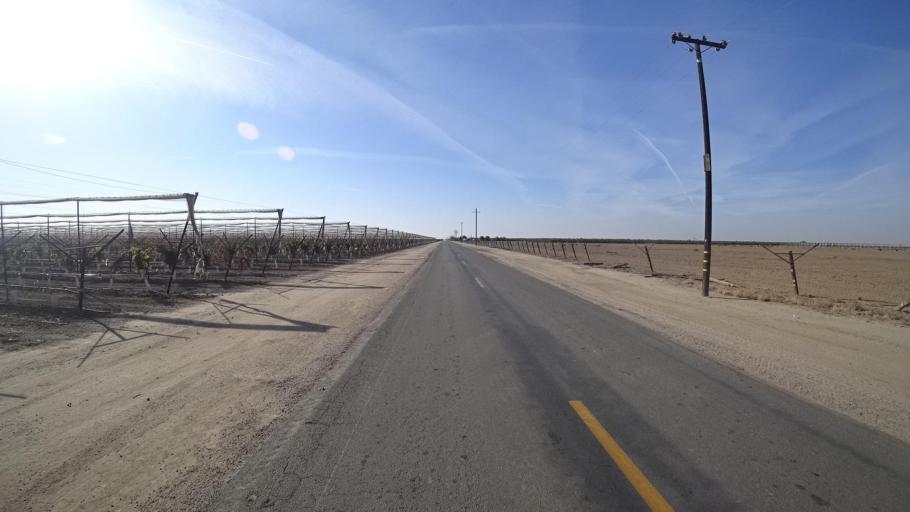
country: US
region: California
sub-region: Kern County
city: McFarland
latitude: 35.7035
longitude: -119.2639
